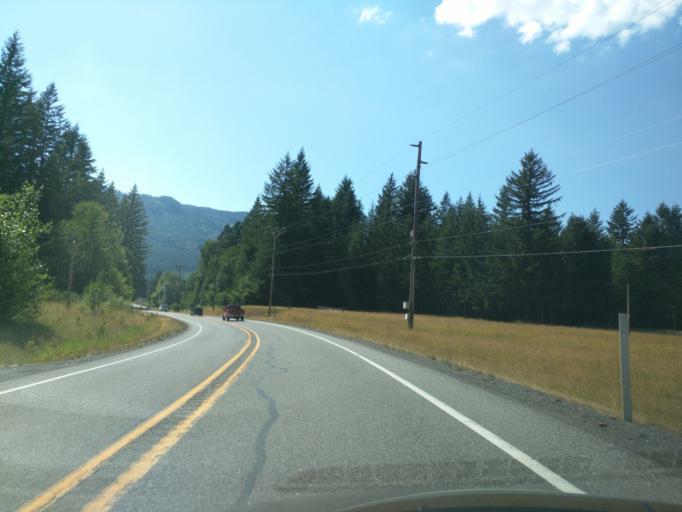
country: US
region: Washington
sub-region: Whatcom County
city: Peaceful Valley
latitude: 48.9170
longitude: -122.1241
